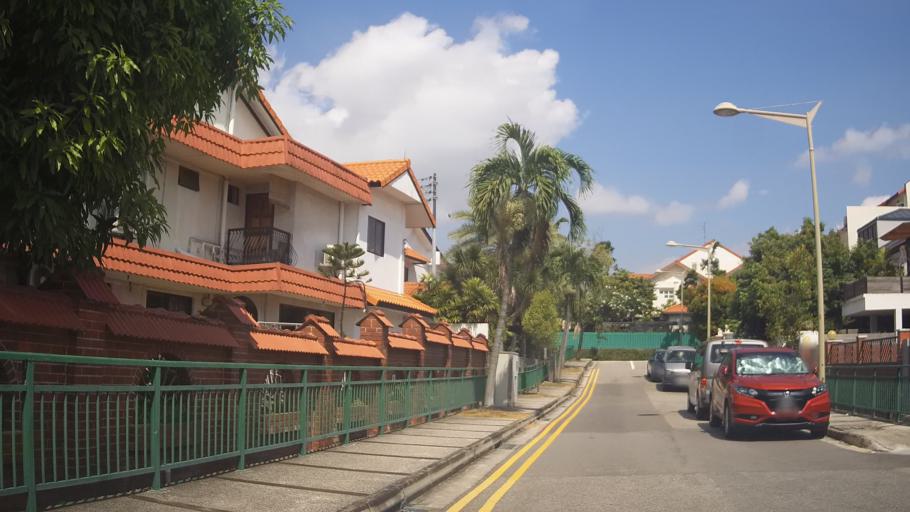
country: SG
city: Singapore
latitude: 1.3292
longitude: 103.9484
